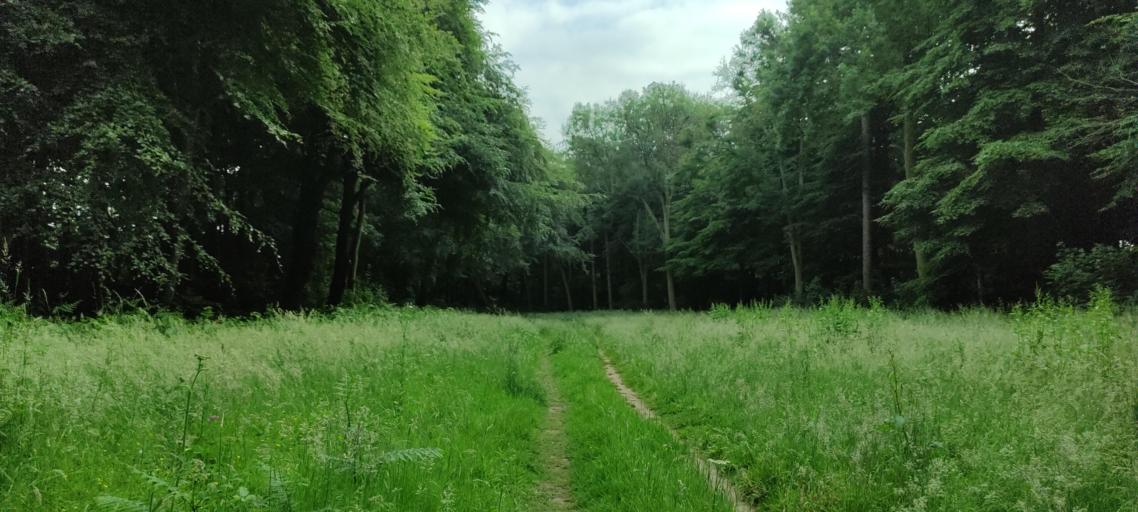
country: GB
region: England
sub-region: Lincolnshire
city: Caistor
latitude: 53.5474
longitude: -0.3330
